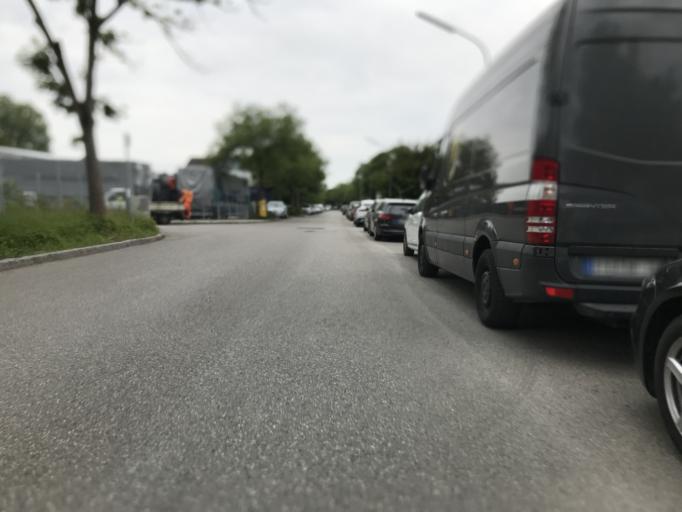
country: DE
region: Bavaria
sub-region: Upper Bavaria
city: Grobenzell
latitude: 48.1893
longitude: 11.3827
